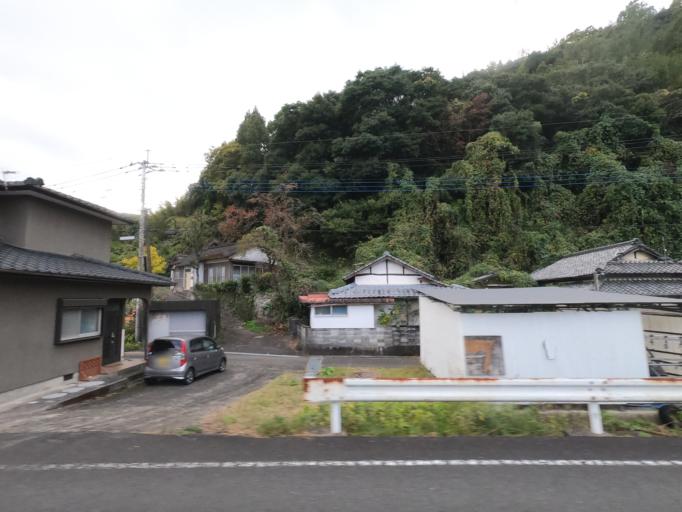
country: JP
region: Kumamoto
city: Minamata
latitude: 32.2646
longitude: 130.5070
